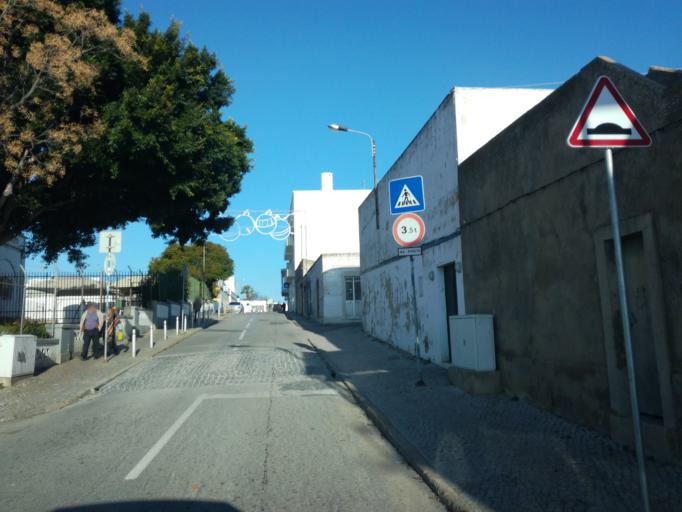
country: PT
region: Faro
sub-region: Olhao
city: Laranjeiro
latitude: 37.0540
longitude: -7.7485
